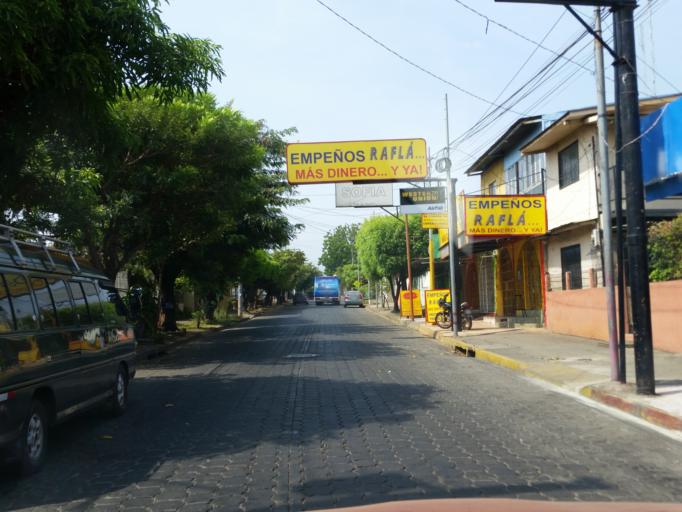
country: NI
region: Managua
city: Managua
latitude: 12.1243
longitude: -86.2971
